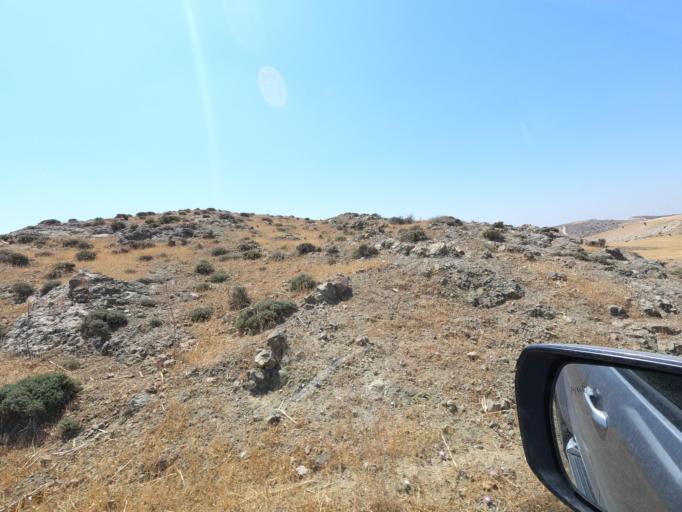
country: CY
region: Larnaka
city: Troulloi
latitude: 35.0003
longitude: 33.6155
